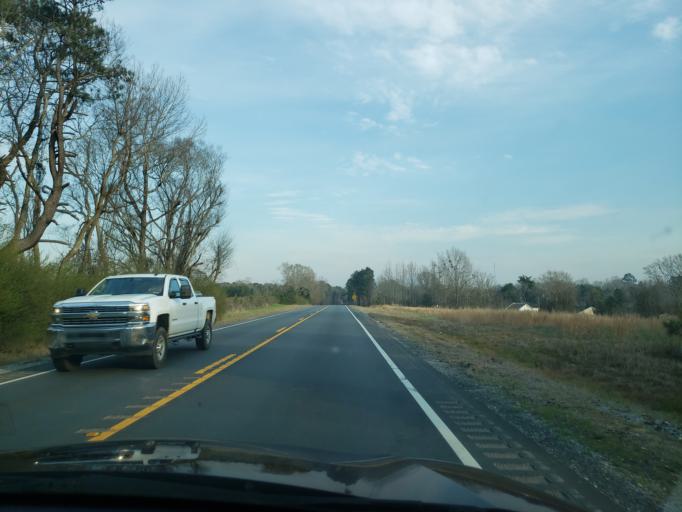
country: US
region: Alabama
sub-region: Hale County
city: Moundville
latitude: 32.8931
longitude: -87.6167
